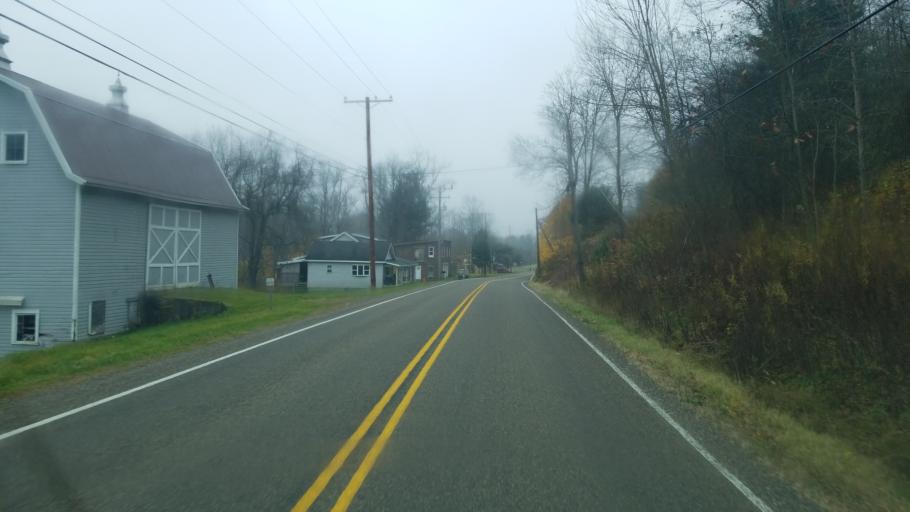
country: US
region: Pennsylvania
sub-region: McKean County
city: Smethport
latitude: 41.8937
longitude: -78.5095
